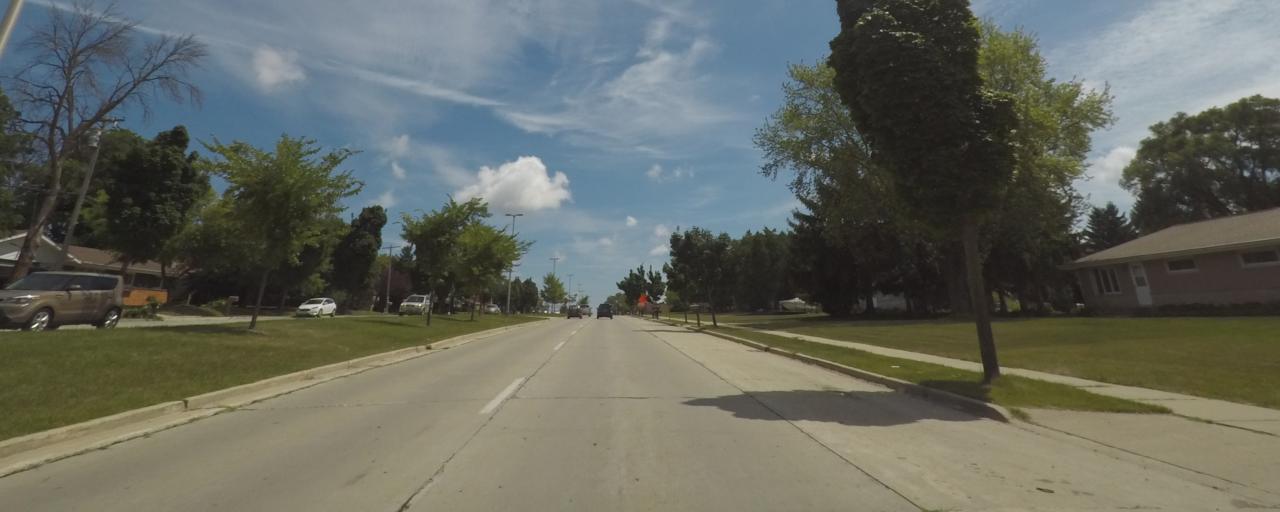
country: US
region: Wisconsin
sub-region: Milwaukee County
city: Greenfield
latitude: 42.9592
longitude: -88.0026
